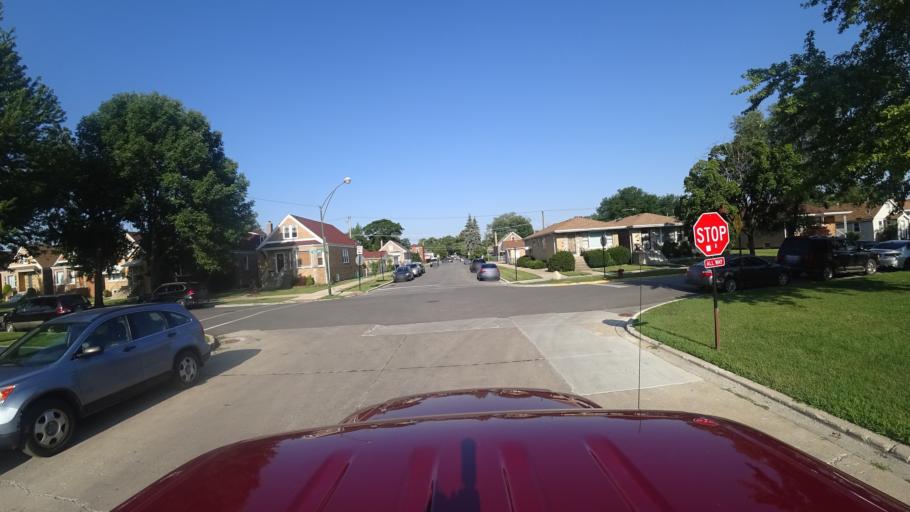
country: US
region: Illinois
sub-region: Cook County
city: Cicero
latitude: 41.7970
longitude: -87.7145
